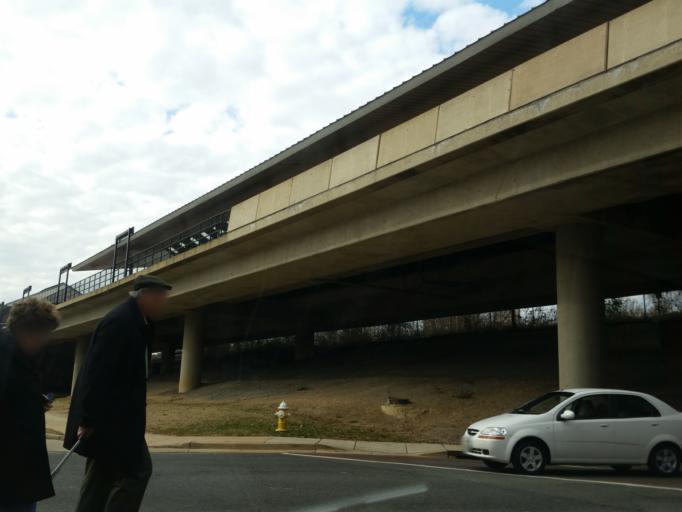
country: US
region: Virginia
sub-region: City of Alexandria
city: Alexandria
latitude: 38.8072
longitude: -77.0598
